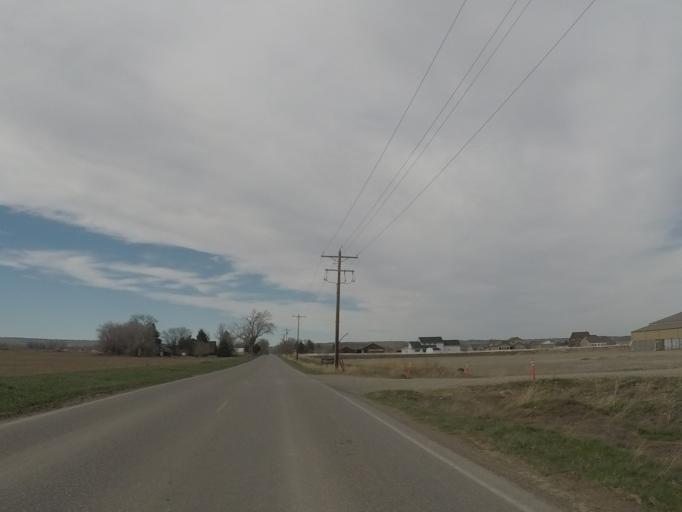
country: US
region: Montana
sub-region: Yellowstone County
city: Laurel
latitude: 45.7204
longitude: -108.6587
